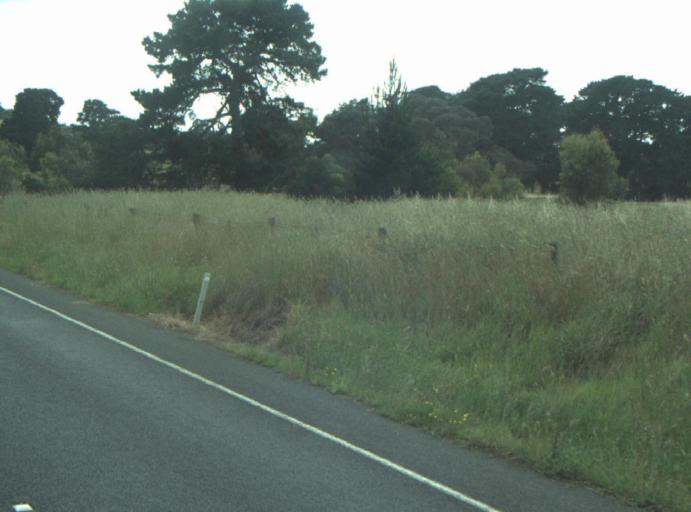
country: AU
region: Victoria
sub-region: Greater Geelong
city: Leopold
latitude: -38.2481
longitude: 144.5045
